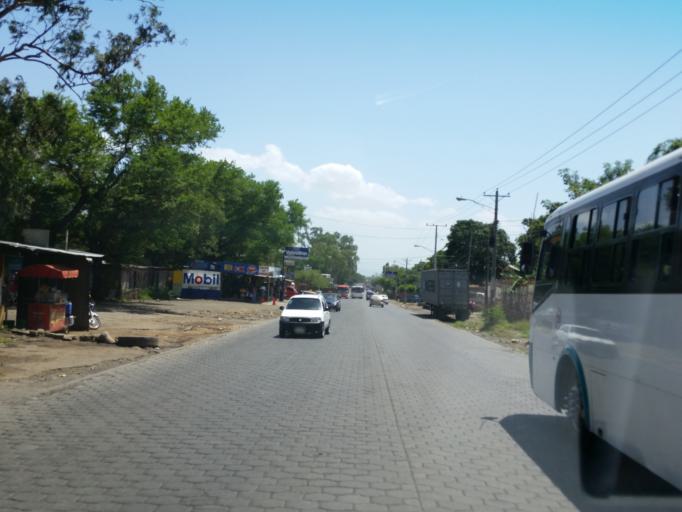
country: NI
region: Managua
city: Managua
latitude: 12.1265
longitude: -86.2040
